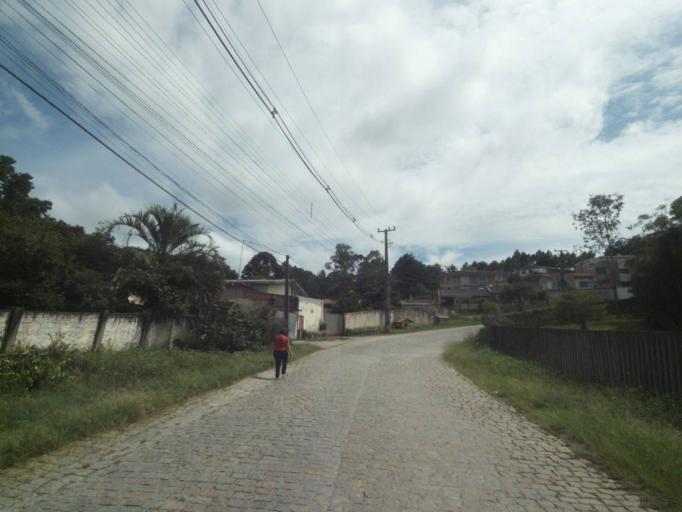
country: BR
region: Parana
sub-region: Campina Grande Do Sul
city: Campina Grande do Sul
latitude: -25.3075
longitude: -49.0475
